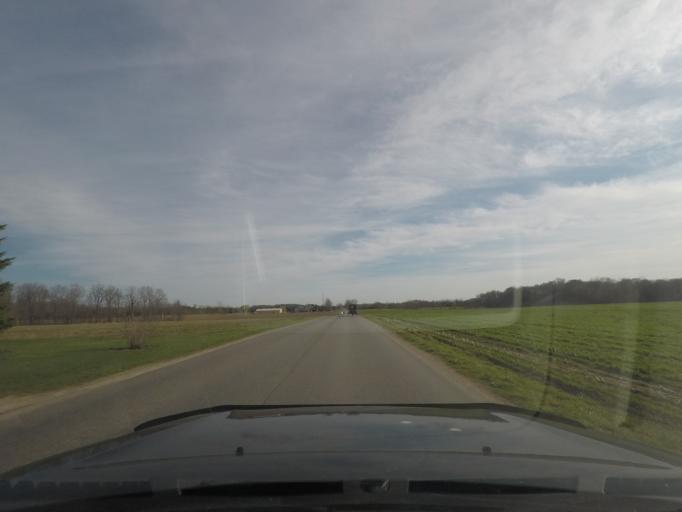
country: US
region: Indiana
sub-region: Elkhart County
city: Dunlap
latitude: 41.5619
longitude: -85.9250
